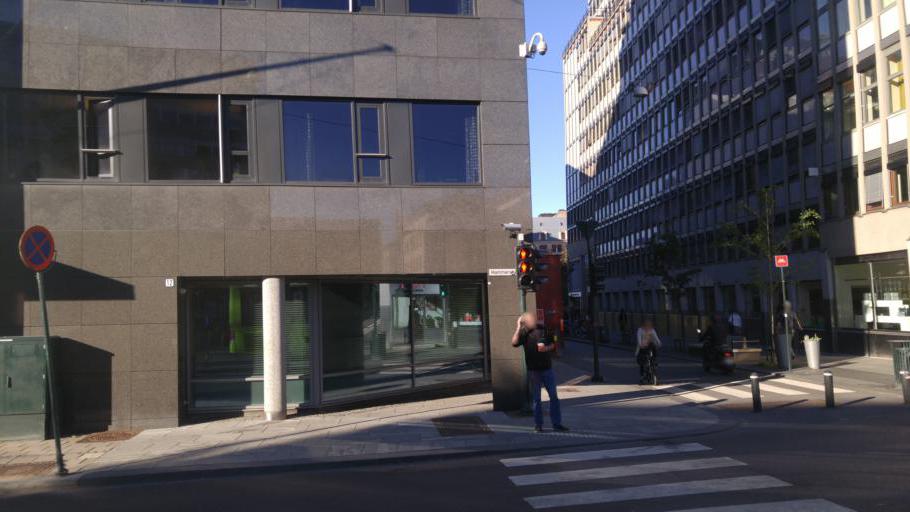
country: NO
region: Oslo
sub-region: Oslo
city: Oslo
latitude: 59.9155
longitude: 10.7508
